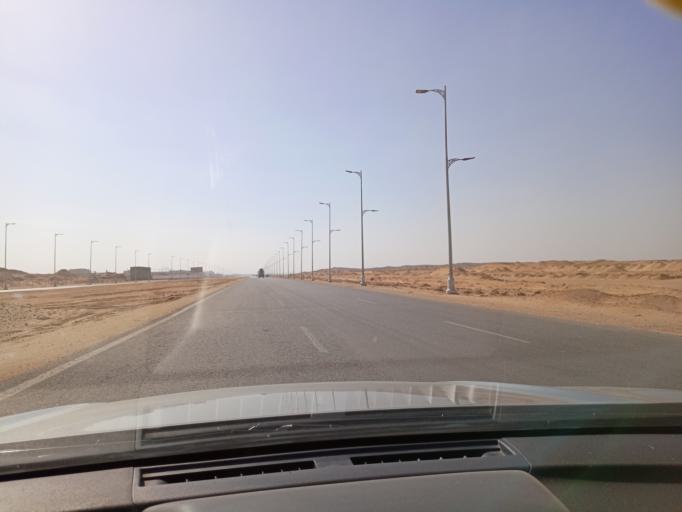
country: EG
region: Muhafazat al Qalyubiyah
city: Al Khankah
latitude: 30.0444
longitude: 31.7113
